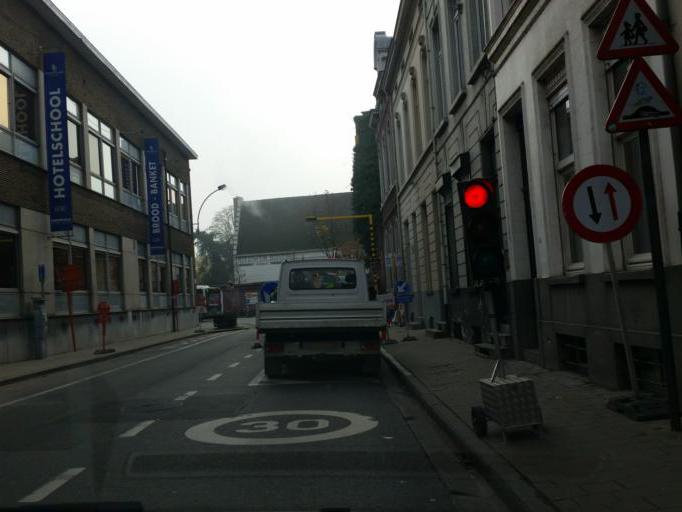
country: BE
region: Flanders
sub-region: Provincie Oost-Vlaanderen
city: Ledeberg
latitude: 51.0490
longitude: 3.7358
